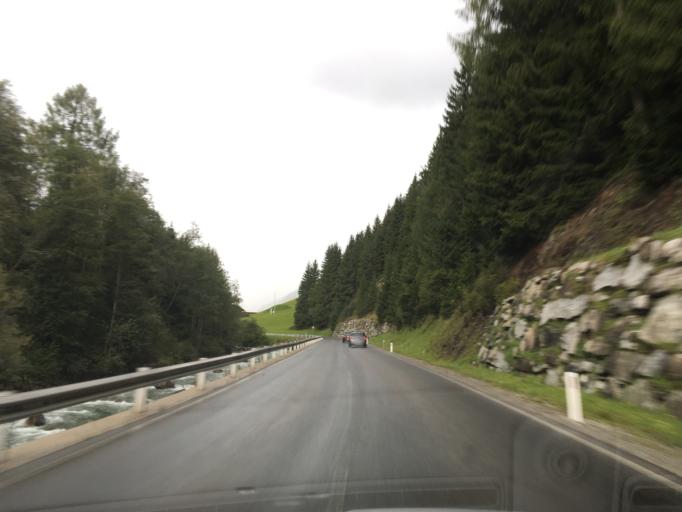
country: AT
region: Tyrol
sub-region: Politischer Bezirk Lienz
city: Innervillgraten
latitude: 46.9169
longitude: 12.3573
